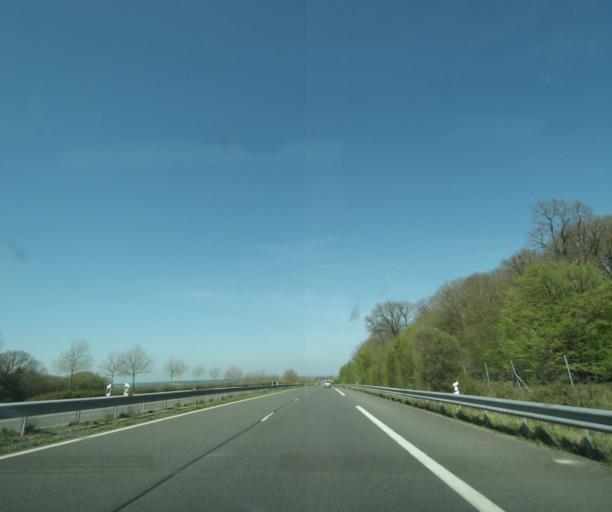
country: FR
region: Bourgogne
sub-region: Departement de la Nievre
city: Chaulgnes
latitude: 47.1191
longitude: 3.0575
